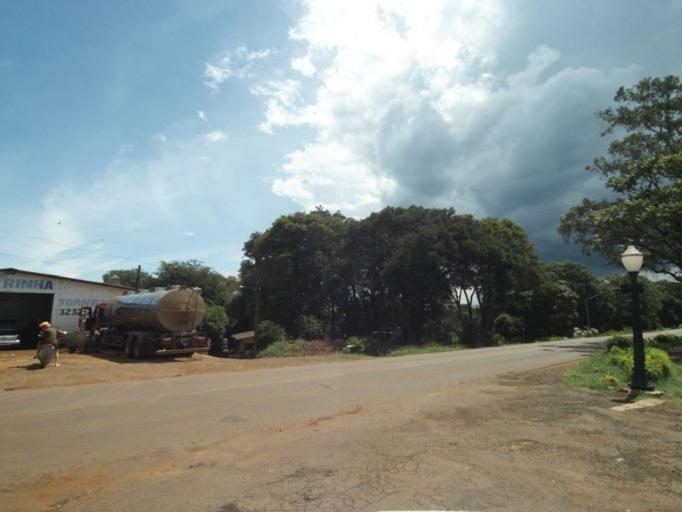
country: BR
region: Parana
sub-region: Guaraniacu
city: Guaraniacu
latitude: -25.0964
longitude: -52.8784
